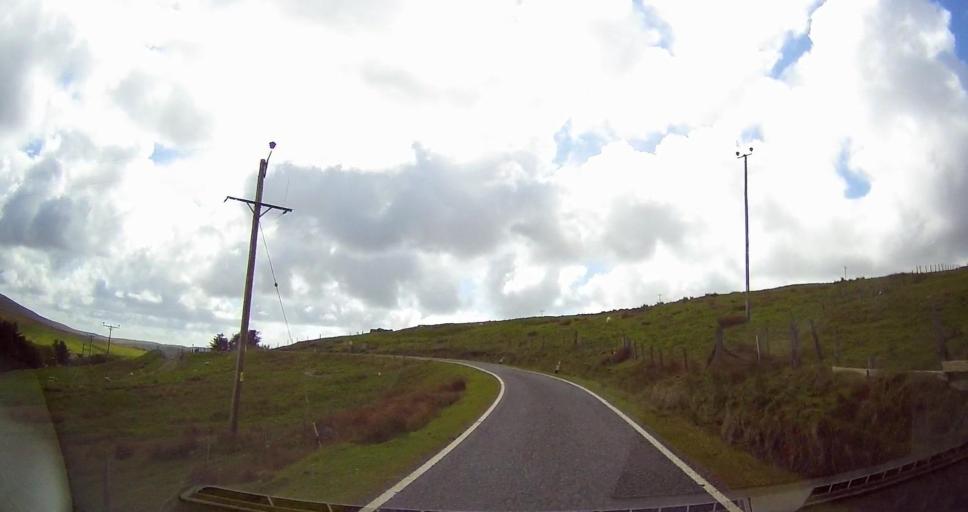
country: GB
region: Scotland
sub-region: Shetland Islands
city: Lerwick
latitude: 60.5297
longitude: -1.3643
